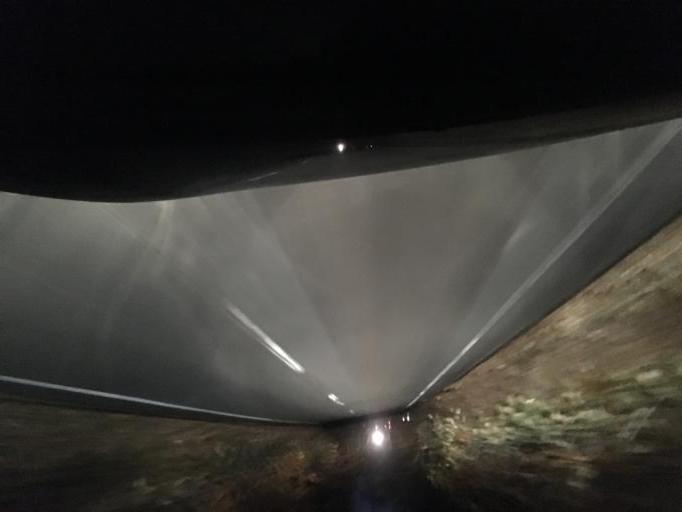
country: JP
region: Akita
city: Yuzawa
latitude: 38.8953
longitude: 140.7371
